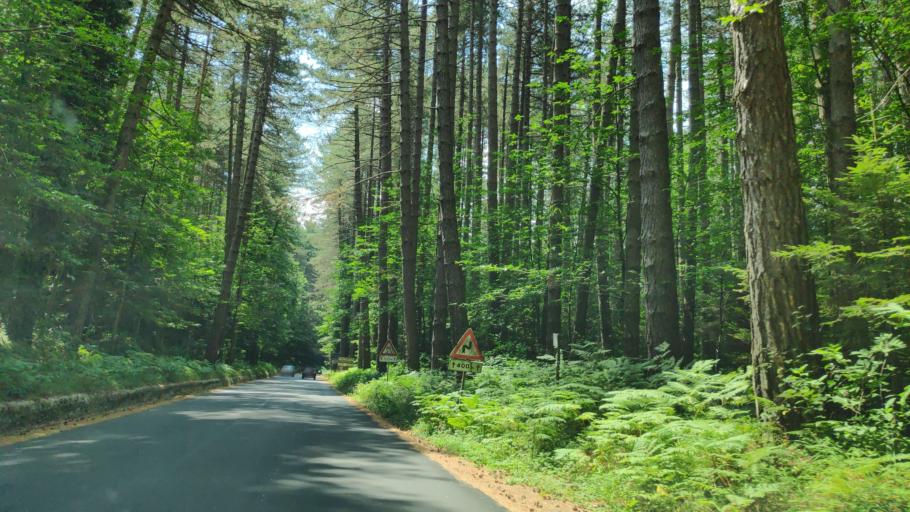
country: IT
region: Calabria
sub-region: Provincia di Vibo-Valentia
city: Mongiana
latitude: 38.5226
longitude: 16.3195
